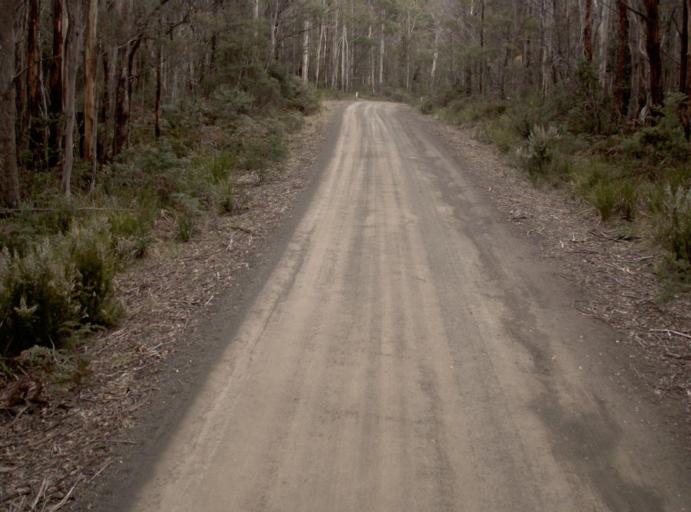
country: AU
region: Tasmania
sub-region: Launceston
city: Newstead
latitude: -41.3962
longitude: 147.3046
